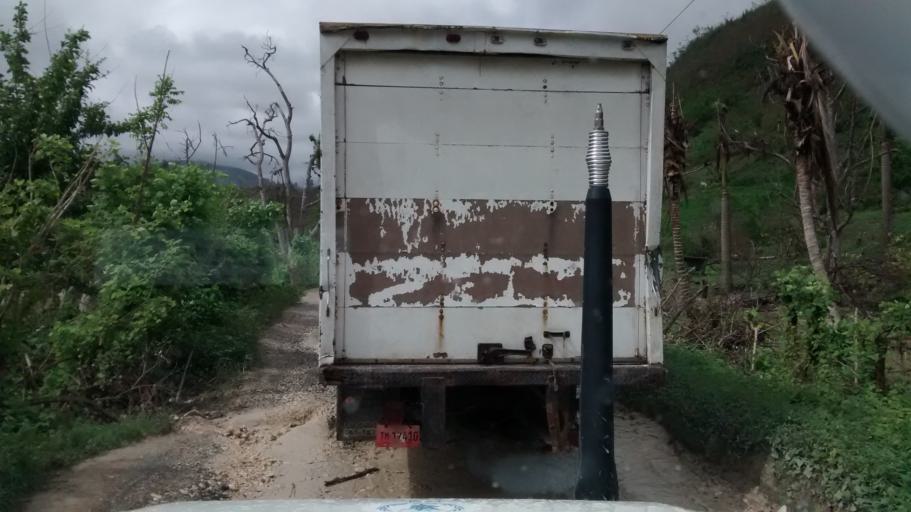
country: HT
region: Grandans
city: Jeremie
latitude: 18.5984
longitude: -74.1764
